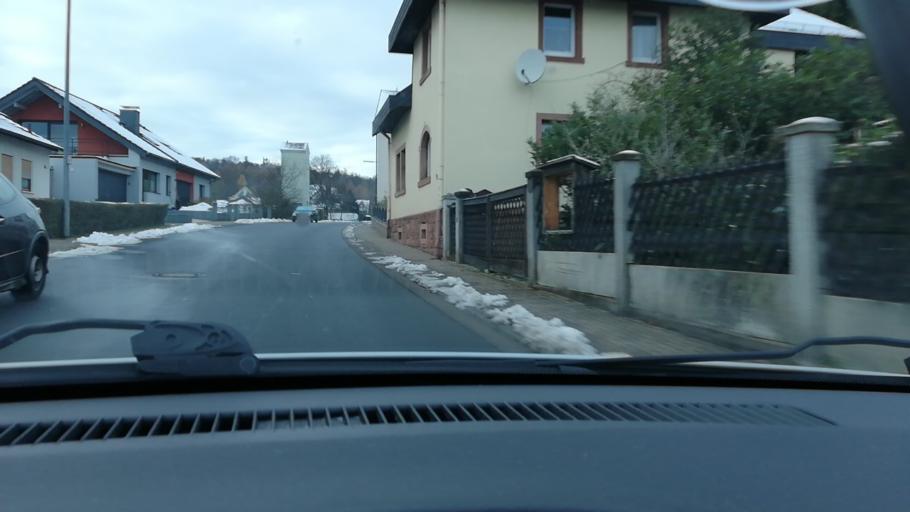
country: DE
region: Bavaria
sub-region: Regierungsbezirk Unterfranken
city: Geiselbach
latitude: 50.1236
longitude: 9.1936
